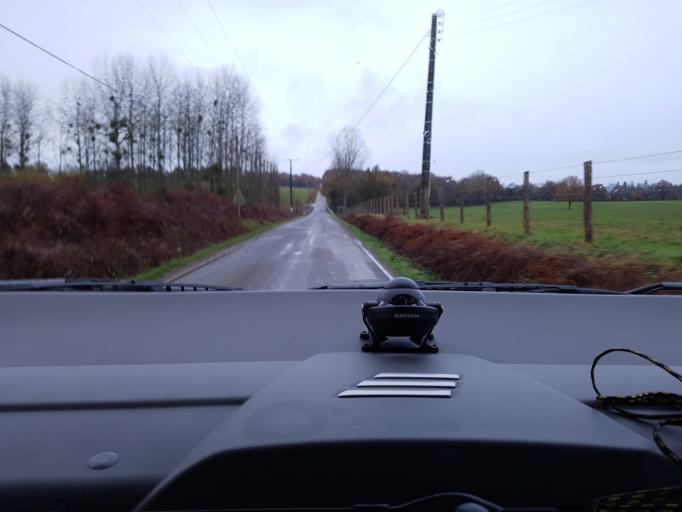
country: FR
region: Brittany
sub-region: Departement d'Ille-et-Vilaine
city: Erbree
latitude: 48.1317
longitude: -1.1441
